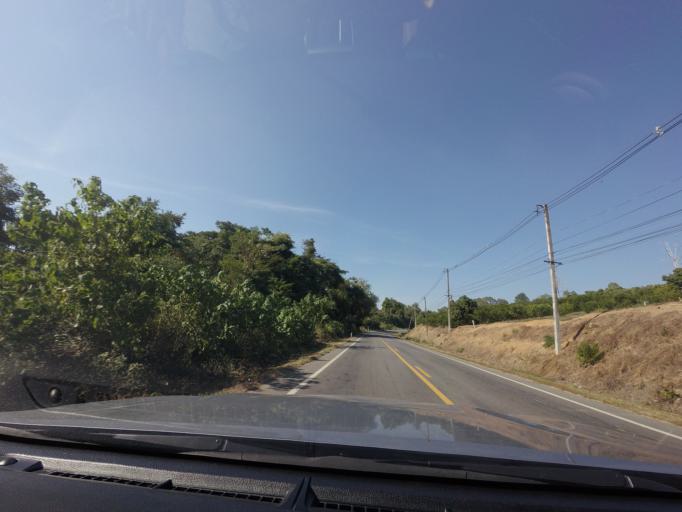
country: TH
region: Sukhothai
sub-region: Amphoe Si Satchanalai
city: Si Satchanalai
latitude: 17.6198
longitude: 99.7060
